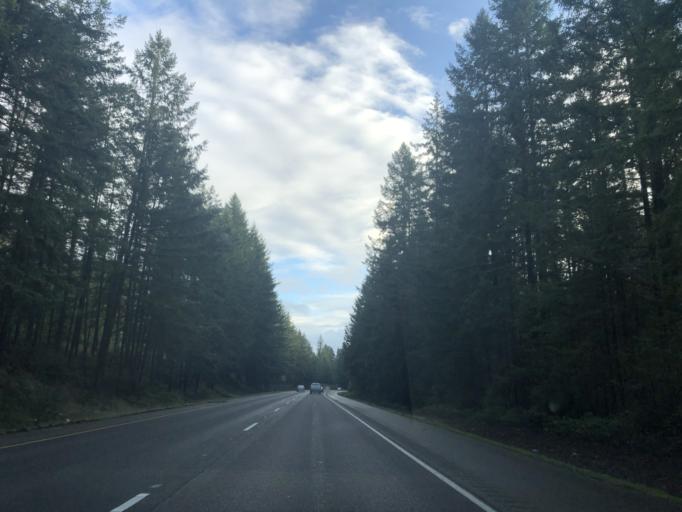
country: US
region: Washington
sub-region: Kitsap County
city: Bethel
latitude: 47.4811
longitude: -122.6282
